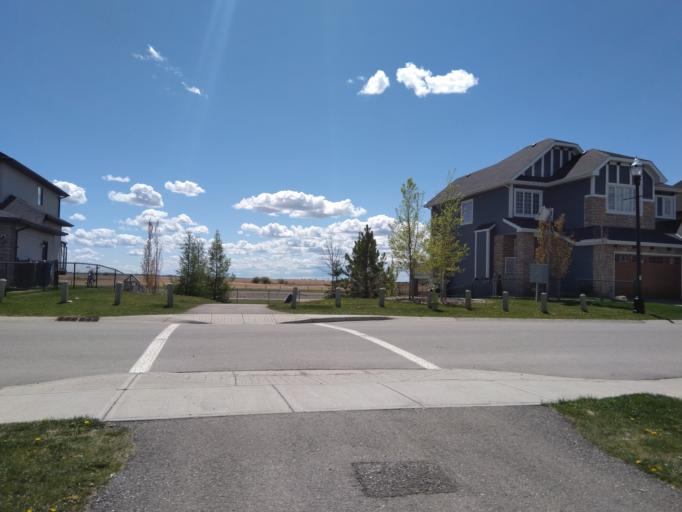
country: CA
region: Alberta
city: Chestermere
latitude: 51.0200
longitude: -113.8347
